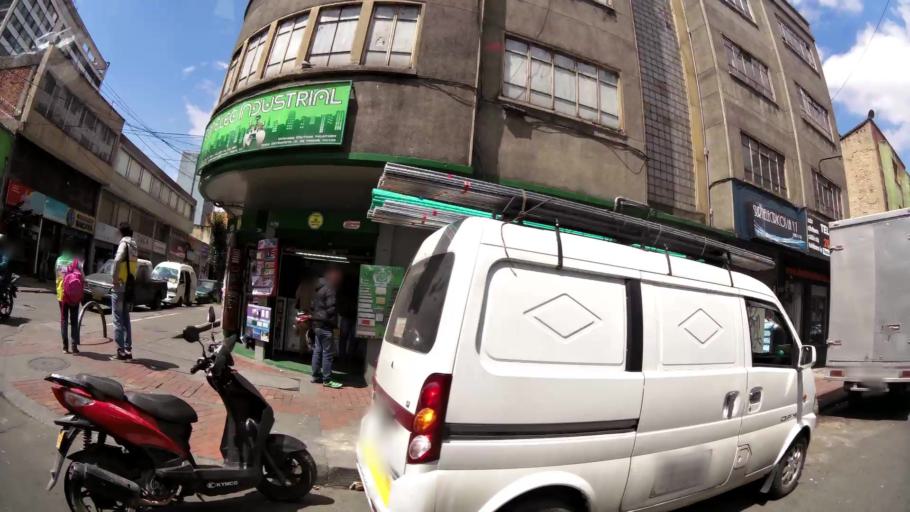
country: CO
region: Bogota D.C.
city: Bogota
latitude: 4.6058
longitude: -74.0757
